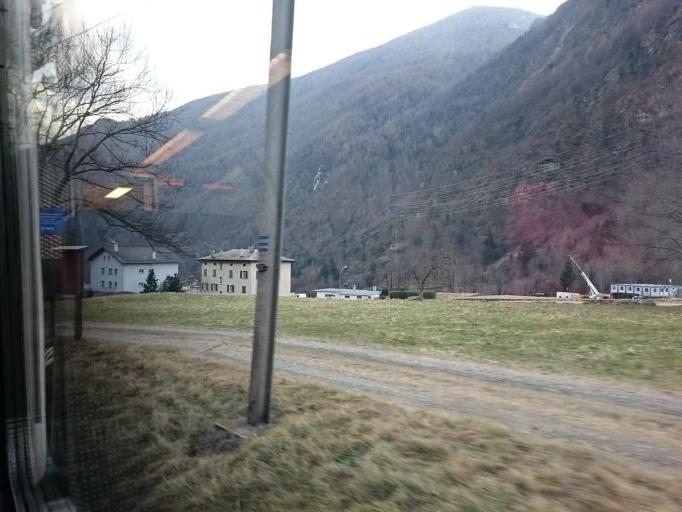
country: CH
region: Grisons
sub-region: Bernina District
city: Brusio
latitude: 46.2533
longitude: 10.1280
